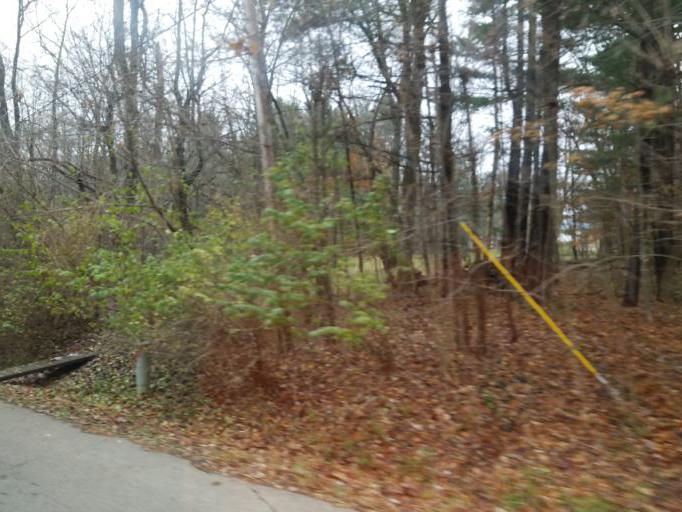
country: US
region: Ohio
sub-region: Richland County
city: Mansfield
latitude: 40.7193
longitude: -82.5330
